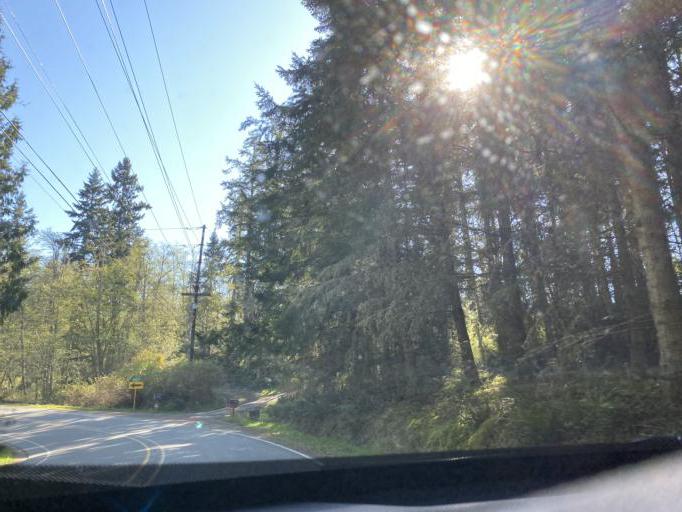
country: US
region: Washington
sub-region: Island County
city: Freeland
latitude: 48.0799
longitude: -122.5841
